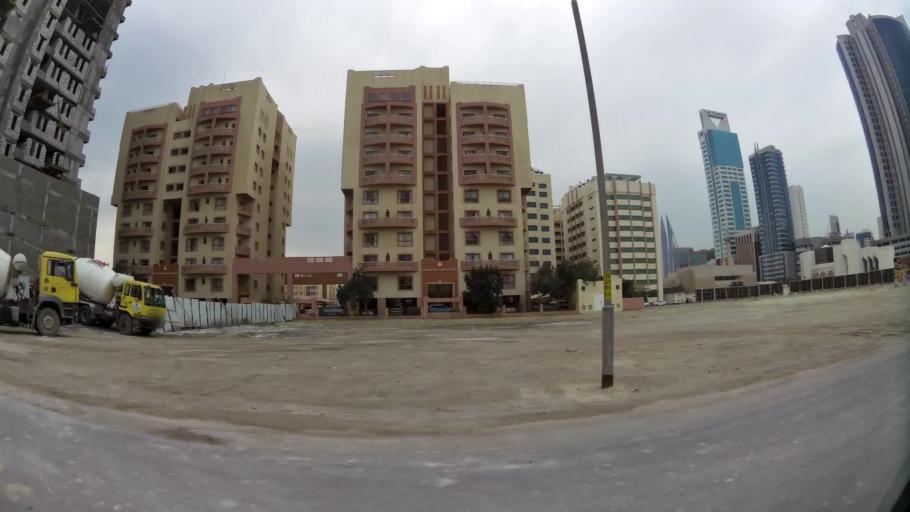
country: BH
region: Muharraq
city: Al Muharraq
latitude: 26.2396
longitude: 50.5943
